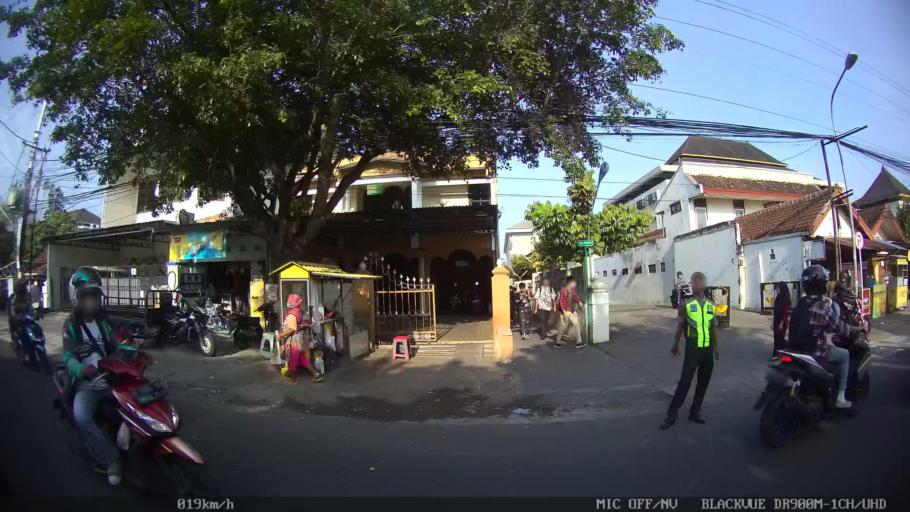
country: ID
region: Daerah Istimewa Yogyakarta
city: Depok
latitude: -7.7787
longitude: 110.4150
